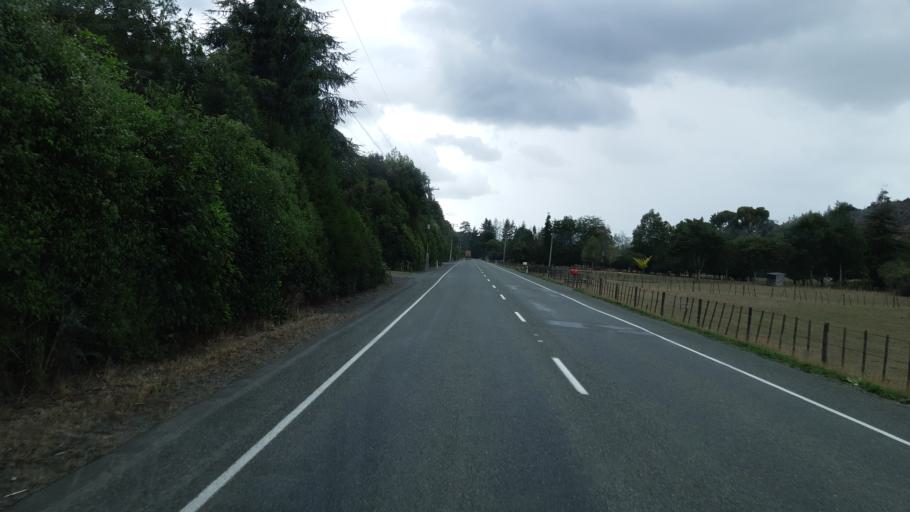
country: NZ
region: Tasman
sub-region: Tasman District
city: Wakefield
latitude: -41.4135
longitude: 173.0154
